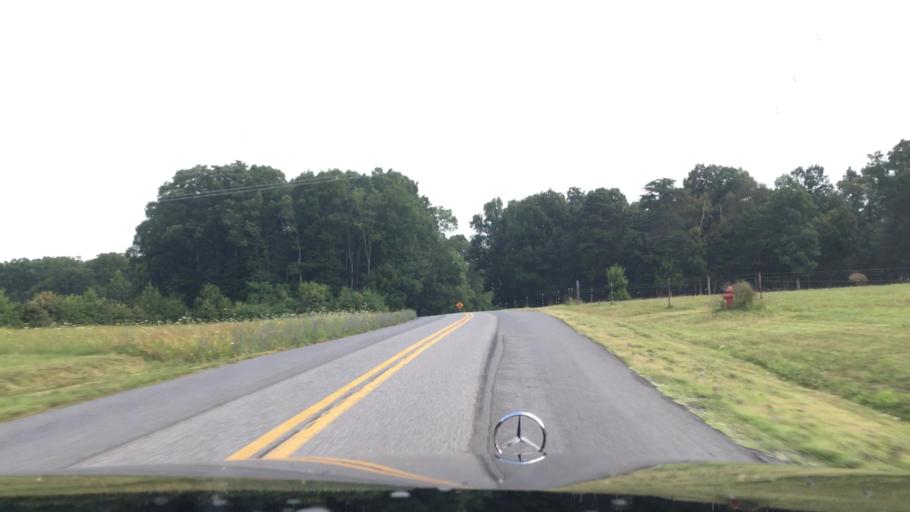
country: US
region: Virginia
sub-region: Campbell County
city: Timberlake
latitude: 37.2825
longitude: -79.3193
